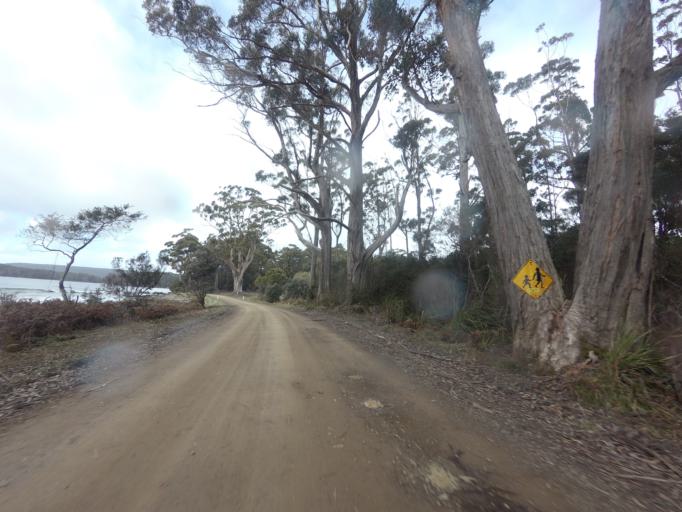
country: AU
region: Tasmania
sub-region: Huon Valley
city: Geeveston
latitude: -43.5447
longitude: 146.8895
